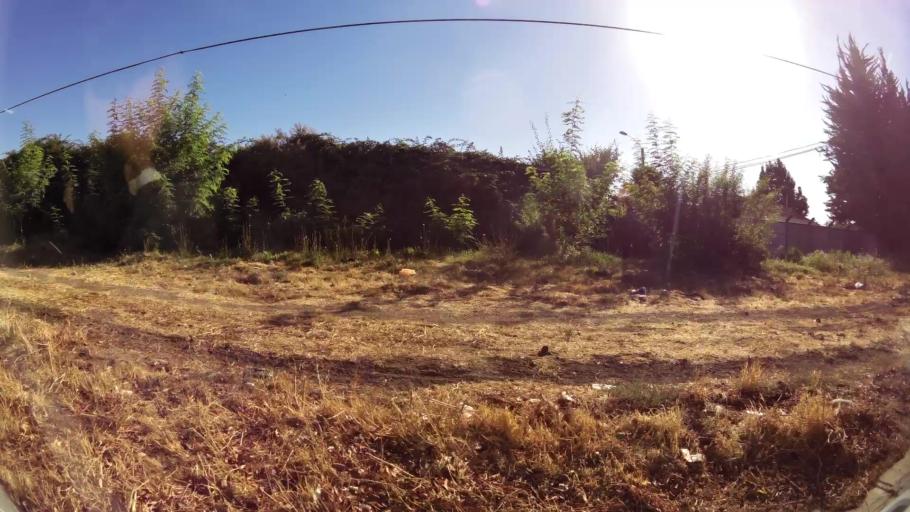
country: CL
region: O'Higgins
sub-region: Provincia de Cachapoal
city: Rancagua
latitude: -34.1836
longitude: -70.7288
